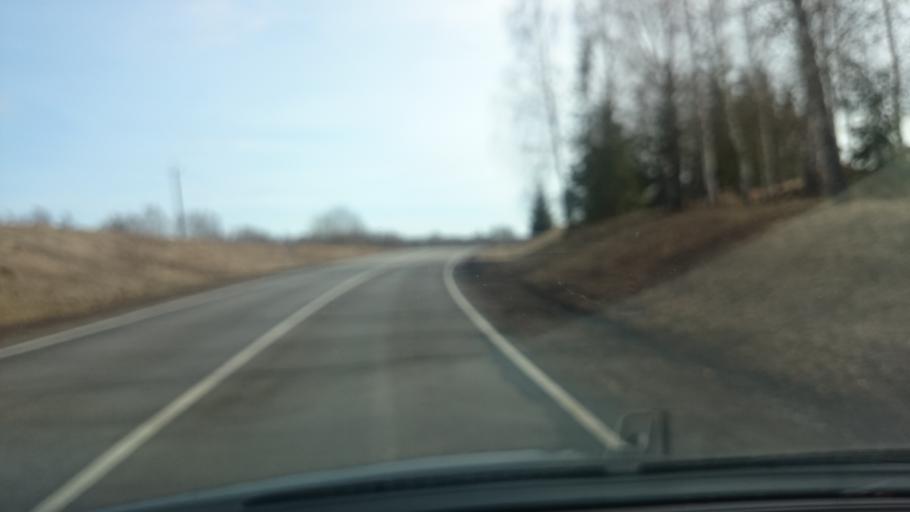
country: EE
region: Jaervamaa
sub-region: Paide linn
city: Paide
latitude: 58.8830
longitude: 25.5168
